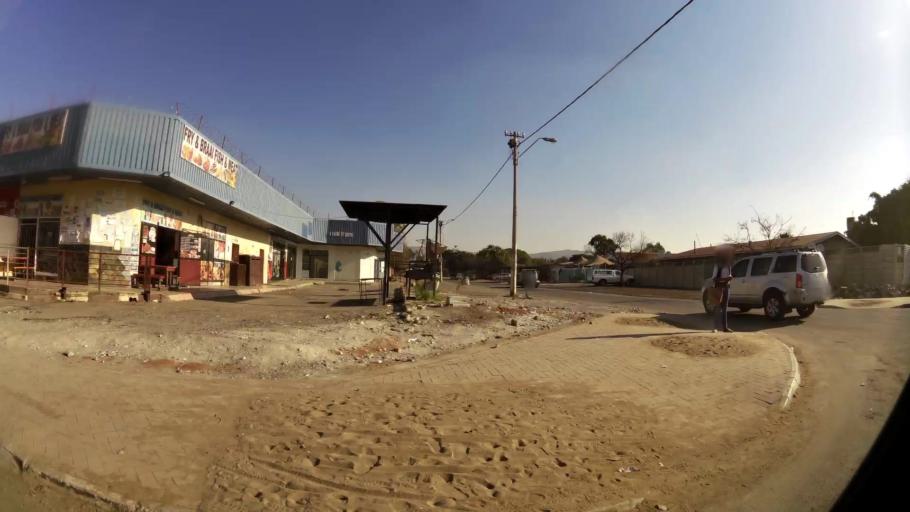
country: ZA
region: North-West
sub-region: Bojanala Platinum District Municipality
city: Rustenburg
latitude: -25.6549
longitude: 27.2335
